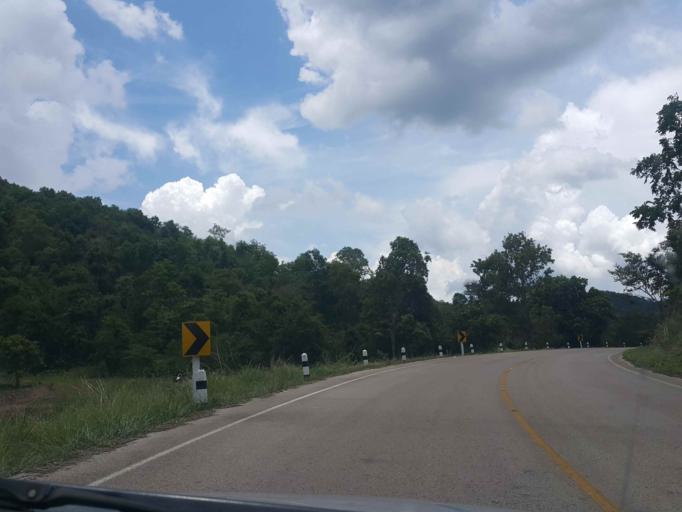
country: TH
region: Phayao
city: Chiang Muan
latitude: 18.9174
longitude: 100.1124
